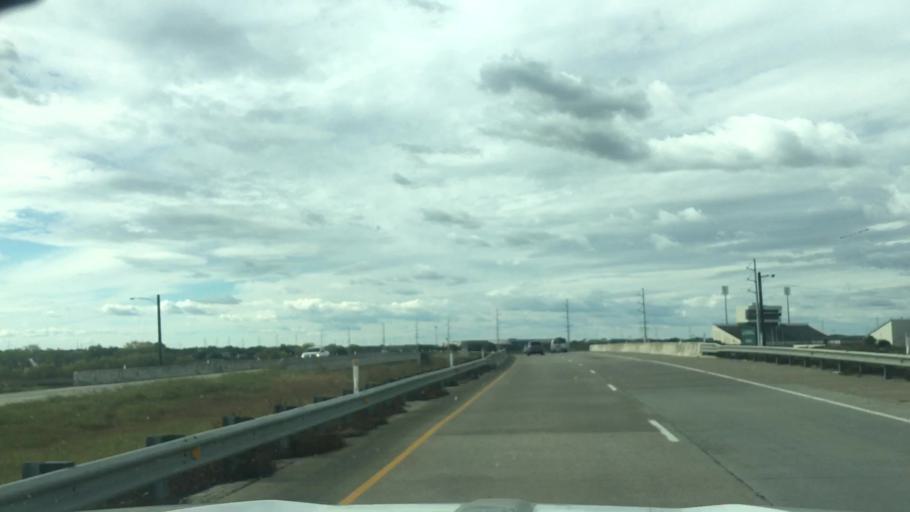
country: US
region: Texas
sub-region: Denton County
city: Denton
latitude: 33.2577
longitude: -97.1090
